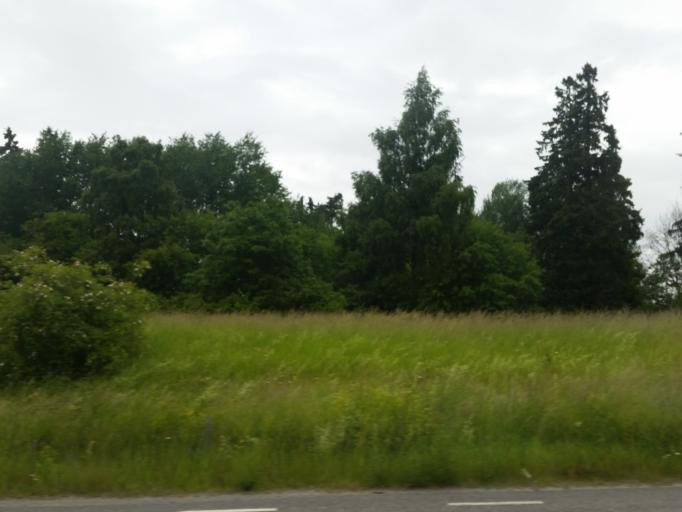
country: SE
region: Stockholm
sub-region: Stockholms Kommun
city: Kista
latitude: 59.4103
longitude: 17.8949
